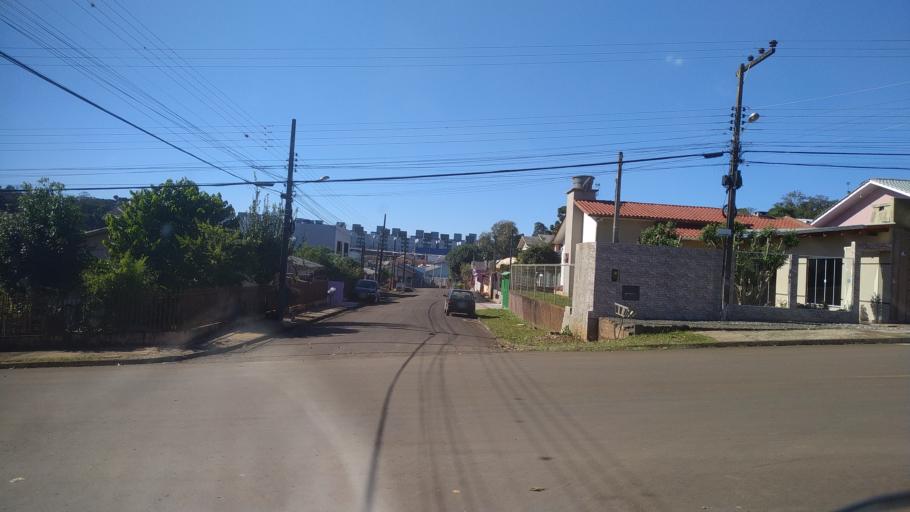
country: BR
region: Santa Catarina
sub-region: Chapeco
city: Chapeco
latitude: -27.1044
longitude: -52.6803
